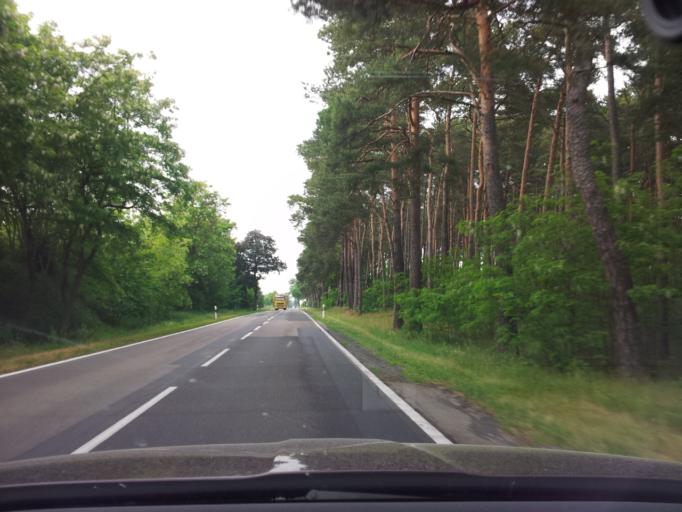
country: DE
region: Brandenburg
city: Linthe
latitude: 52.1415
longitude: 12.7898
